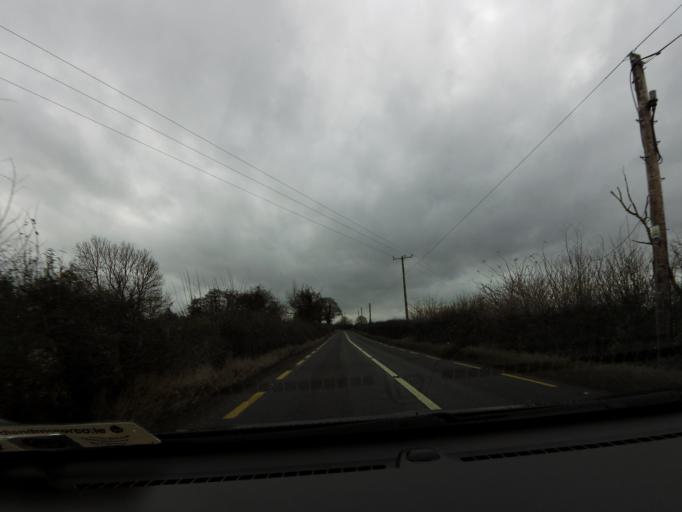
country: IE
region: Leinster
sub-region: Kilkenny
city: Ballyragget
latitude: 52.7538
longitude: -7.3286
